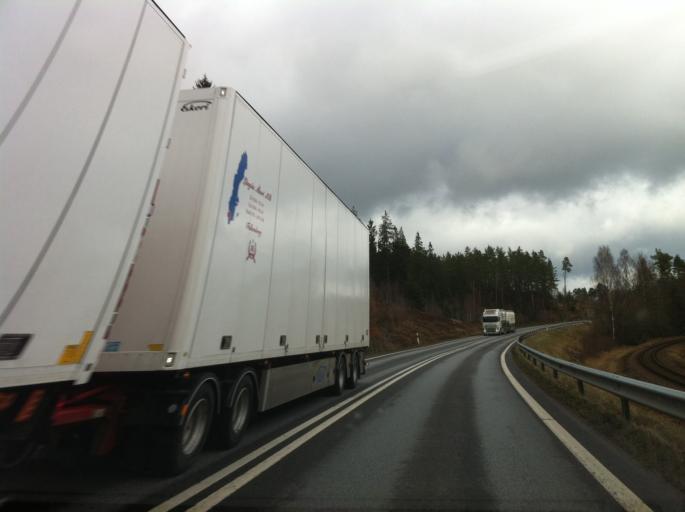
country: SE
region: Halland
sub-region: Halmstads Kommun
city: Oskarstrom
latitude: 56.8391
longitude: 12.9828
